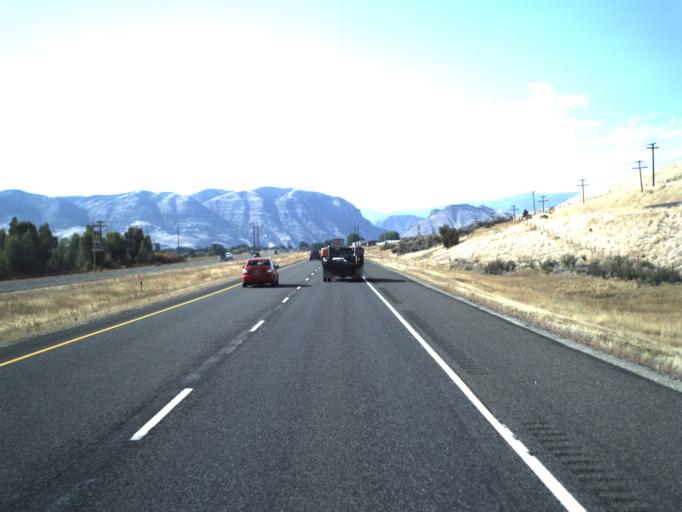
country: US
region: Utah
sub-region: Summit County
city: Coalville
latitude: 41.0051
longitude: -111.4744
